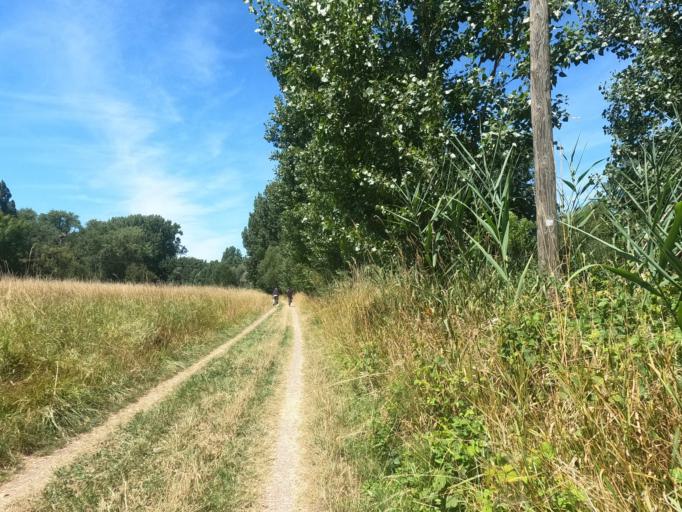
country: DE
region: Hesse
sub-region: Regierungsbezirk Darmstadt
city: Ginsheim-Gustavsburg
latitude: 49.9608
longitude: 8.3455
